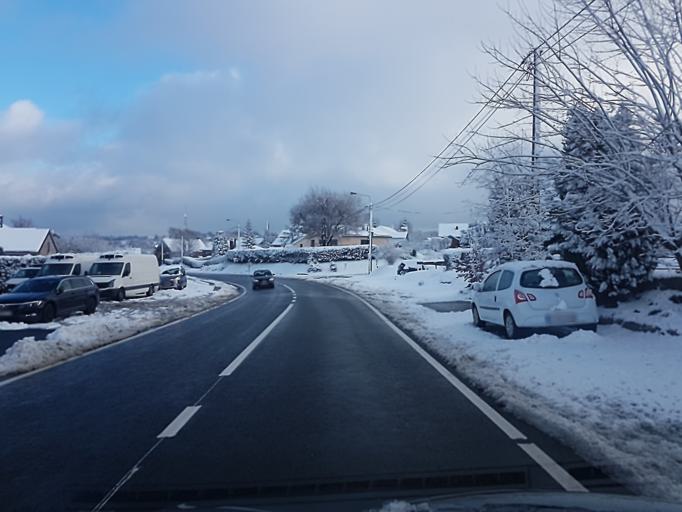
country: BE
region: Wallonia
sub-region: Province de Liege
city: Jalhay
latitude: 50.5589
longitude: 5.9570
